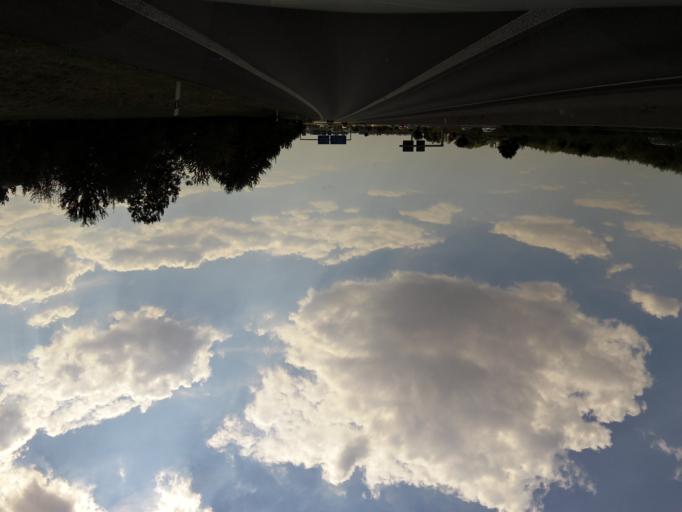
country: DE
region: Hesse
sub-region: Regierungsbezirk Darmstadt
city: Bad Homburg vor der Hoehe
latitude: 50.1992
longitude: 8.6475
